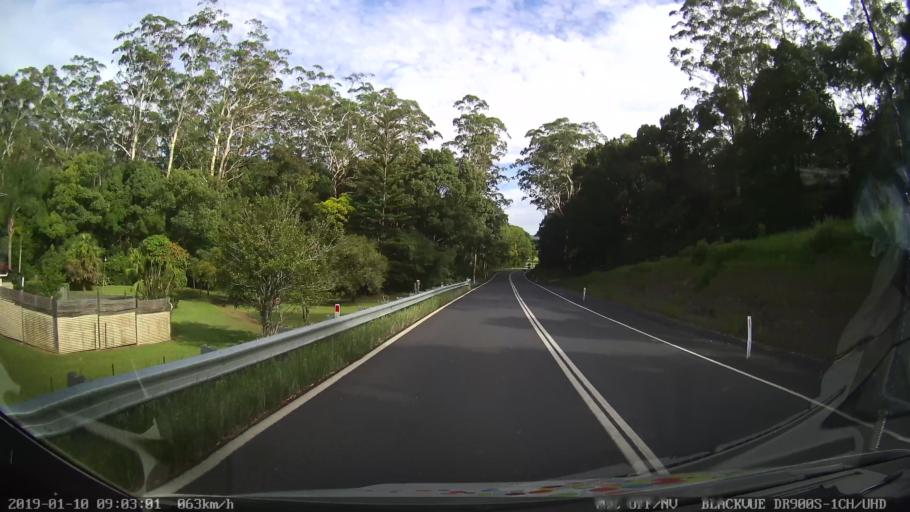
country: AU
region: New South Wales
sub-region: Coffs Harbour
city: Coffs Harbour
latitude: -30.2677
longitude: 153.0490
